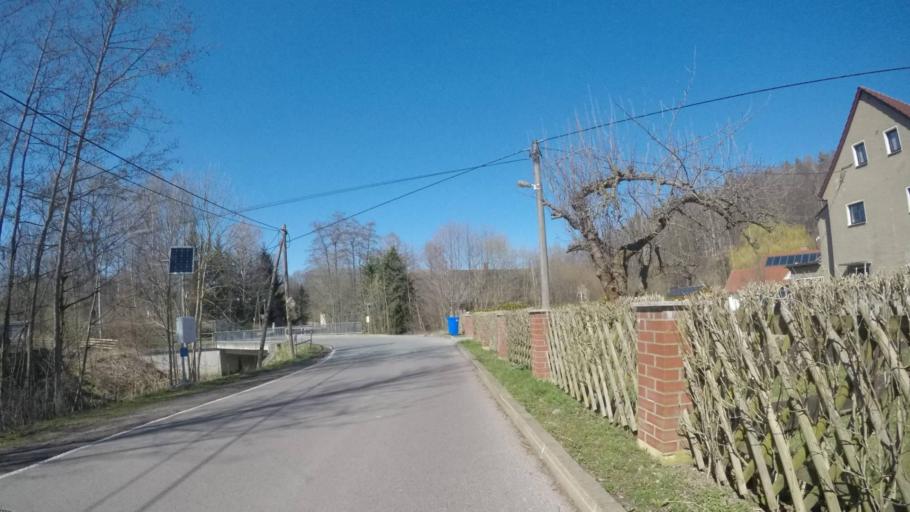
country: DE
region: Saxony
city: Callenberg
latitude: 50.8866
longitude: 12.6616
